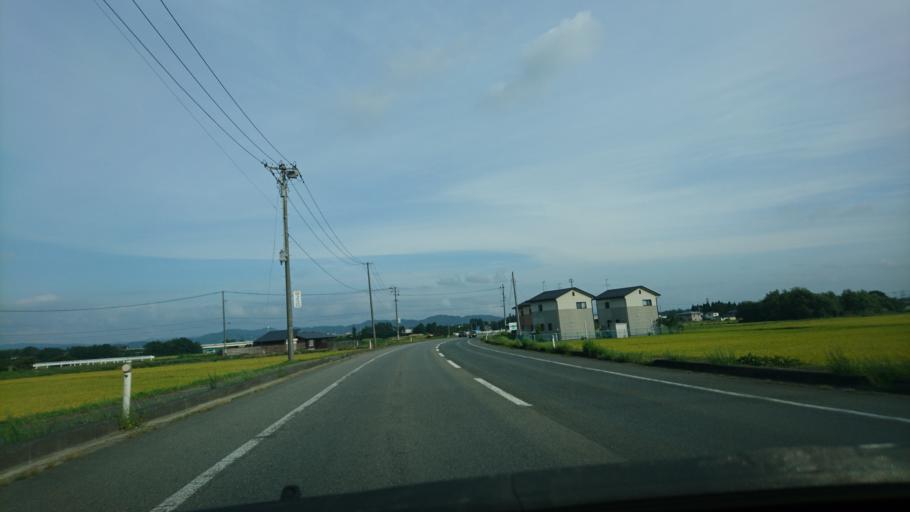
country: JP
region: Iwate
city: Kitakami
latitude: 39.3002
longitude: 141.0796
